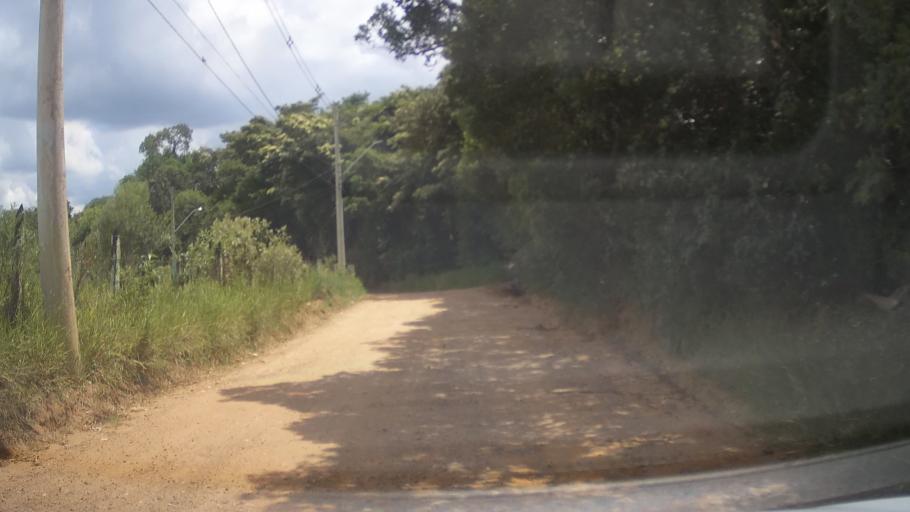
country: BR
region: Sao Paulo
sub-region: Itupeva
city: Itupeva
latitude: -23.1791
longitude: -47.0075
